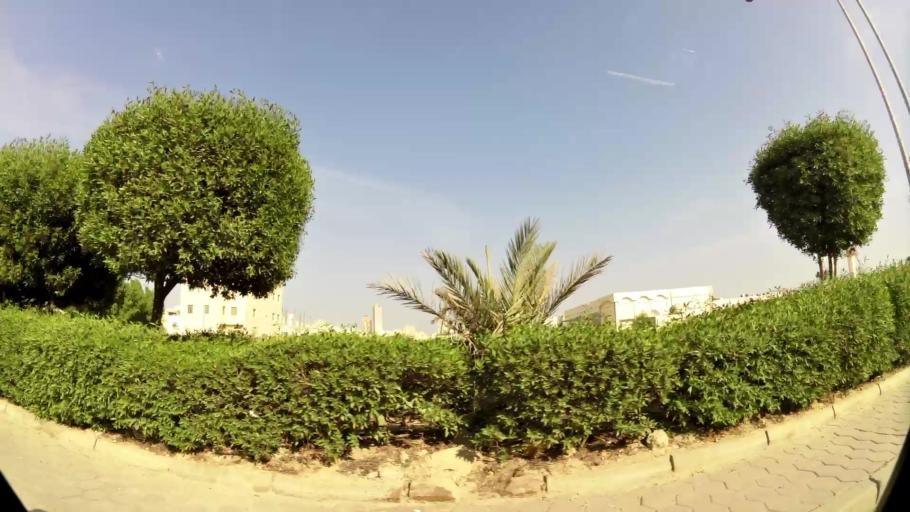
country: KW
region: Al Ahmadi
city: Ar Riqqah
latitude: 29.1555
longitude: 48.1040
